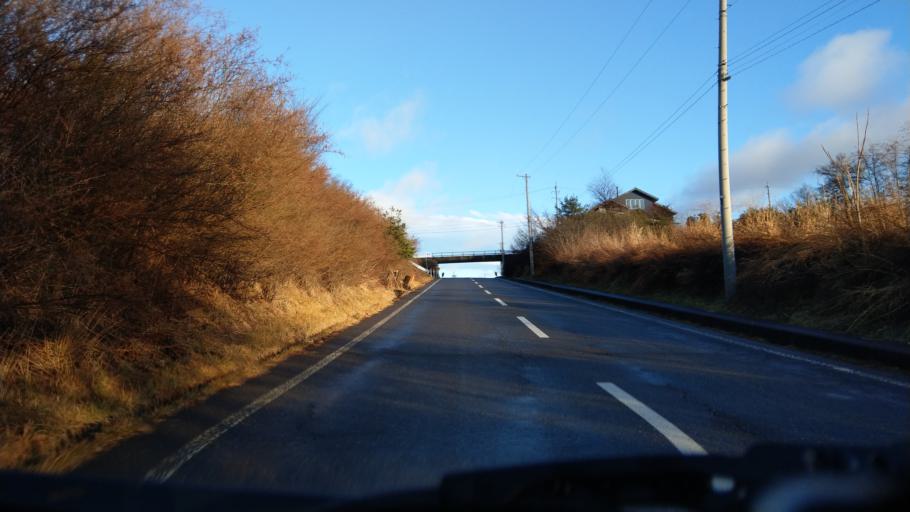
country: JP
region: Nagano
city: Komoro
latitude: 36.3055
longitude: 138.3713
